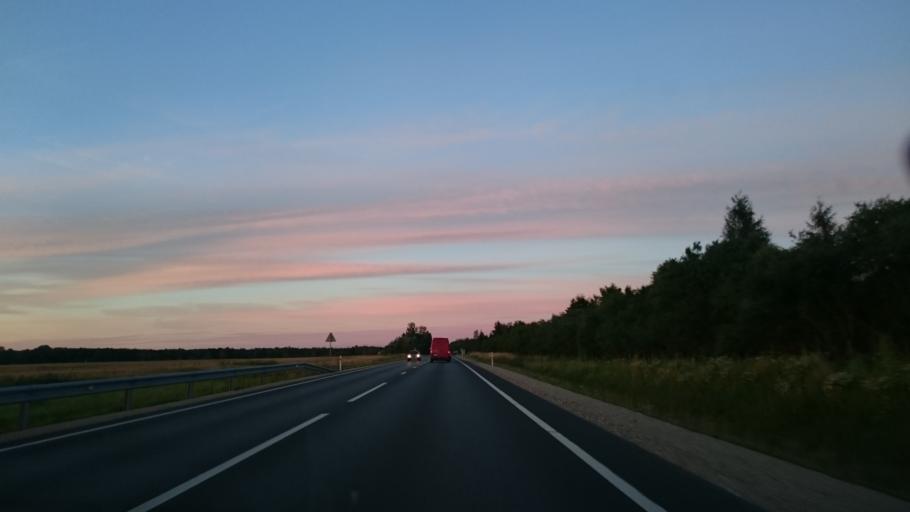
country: LV
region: Dobeles Rajons
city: Dobele
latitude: 56.7425
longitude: 23.2476
